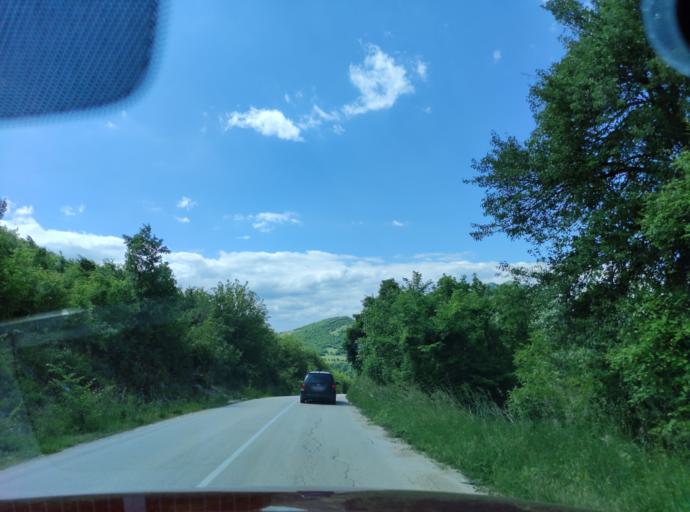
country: BG
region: Vidin
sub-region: Obshtina Ruzhintsi
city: Ruzhintsi
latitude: 43.4959
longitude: 22.7864
